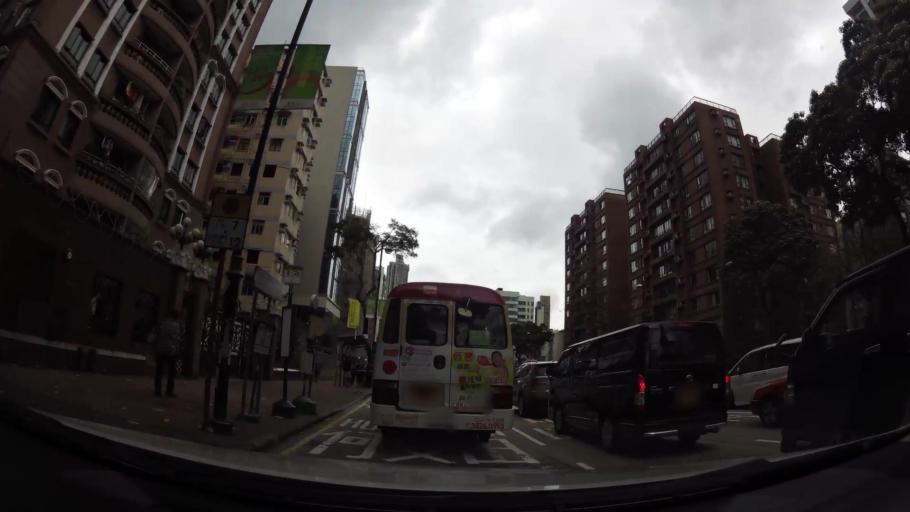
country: HK
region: Kowloon City
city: Kowloon
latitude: 22.3262
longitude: 114.1807
